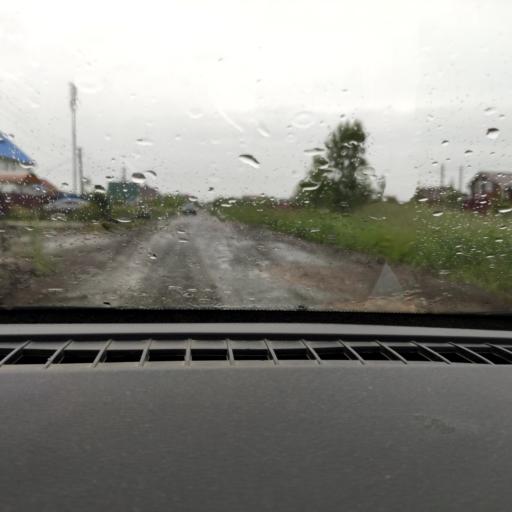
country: RU
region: Perm
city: Perm
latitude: 58.0402
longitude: 56.3728
